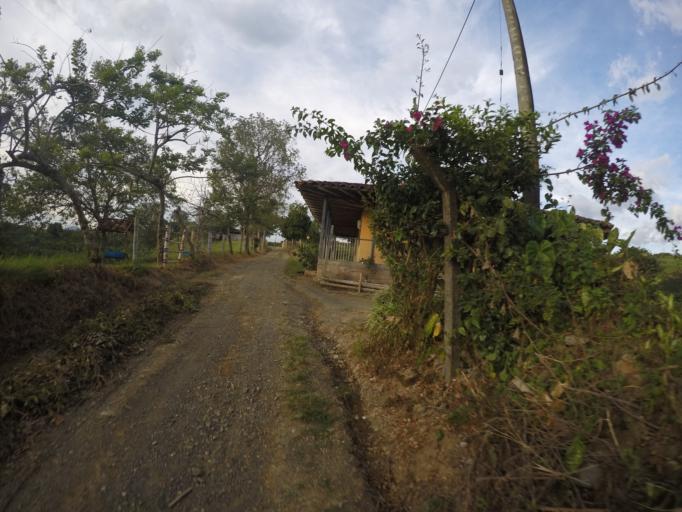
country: CO
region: Valle del Cauca
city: Ulloa
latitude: 4.7128
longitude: -75.7332
